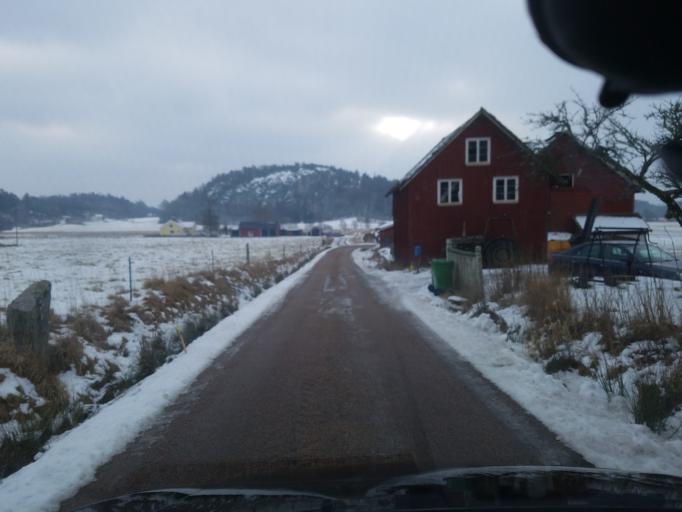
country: SE
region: Vaestra Goetaland
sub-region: Orust
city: Henan
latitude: 58.2909
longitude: 11.6364
